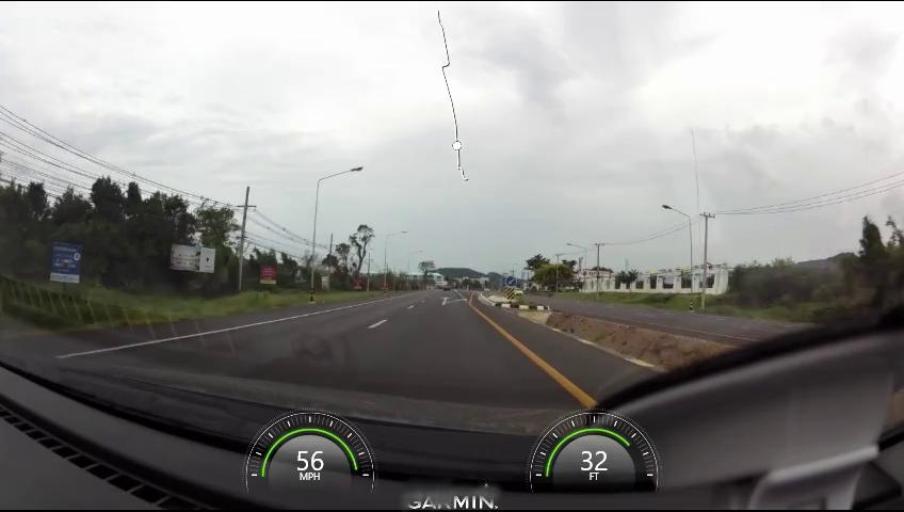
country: TH
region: Prachuap Khiri Khan
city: Hua Hin
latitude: 12.4821
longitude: 99.9709
